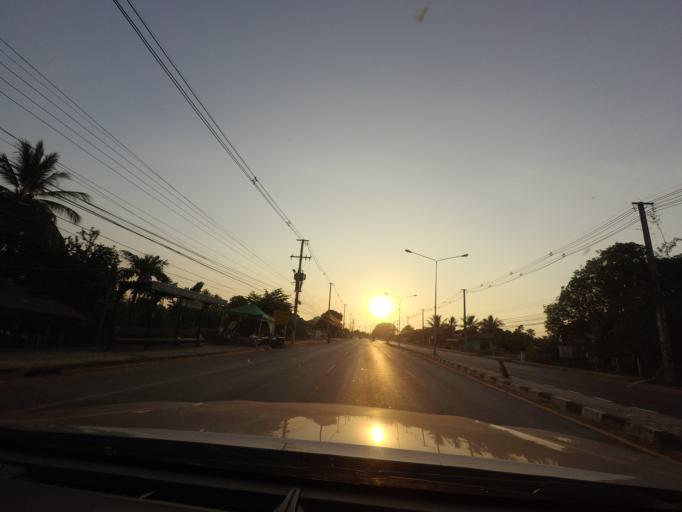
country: TH
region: Sukhothai
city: Si Samrong
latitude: 17.1113
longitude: 99.8462
